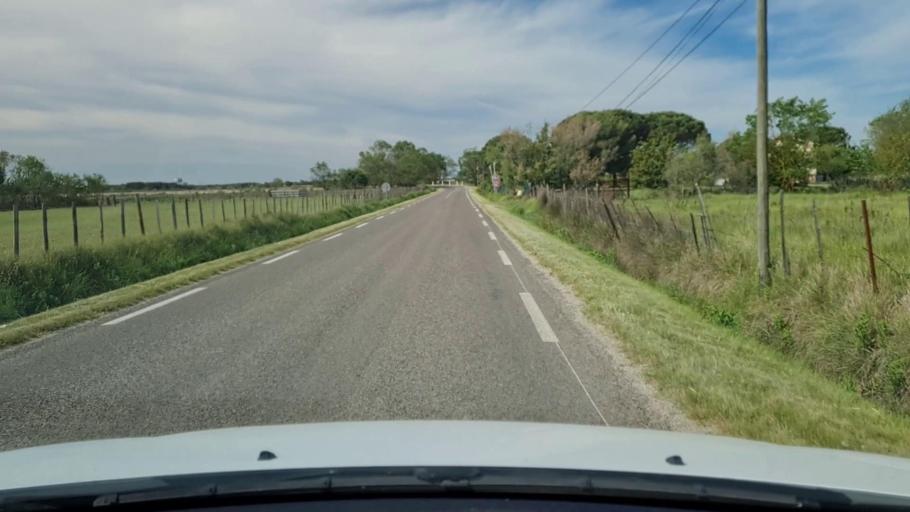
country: FR
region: Languedoc-Roussillon
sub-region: Departement du Gard
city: Aigues-Mortes
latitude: 43.5997
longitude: 4.2093
